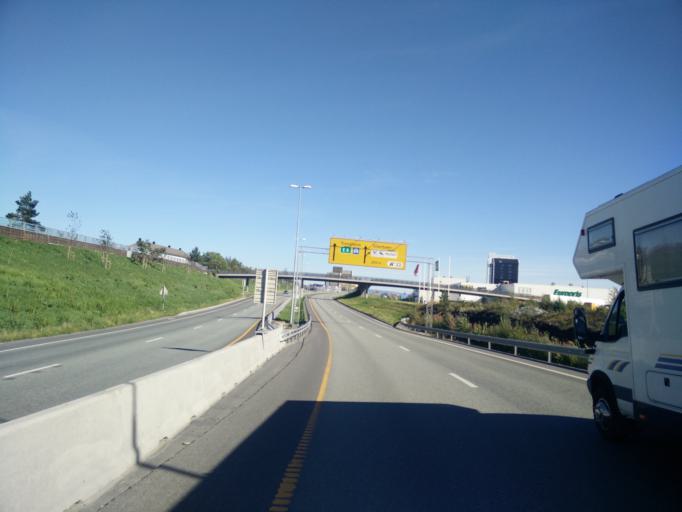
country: NO
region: Sor-Trondelag
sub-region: Trondheim
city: Trondheim
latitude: 63.3544
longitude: 10.3703
